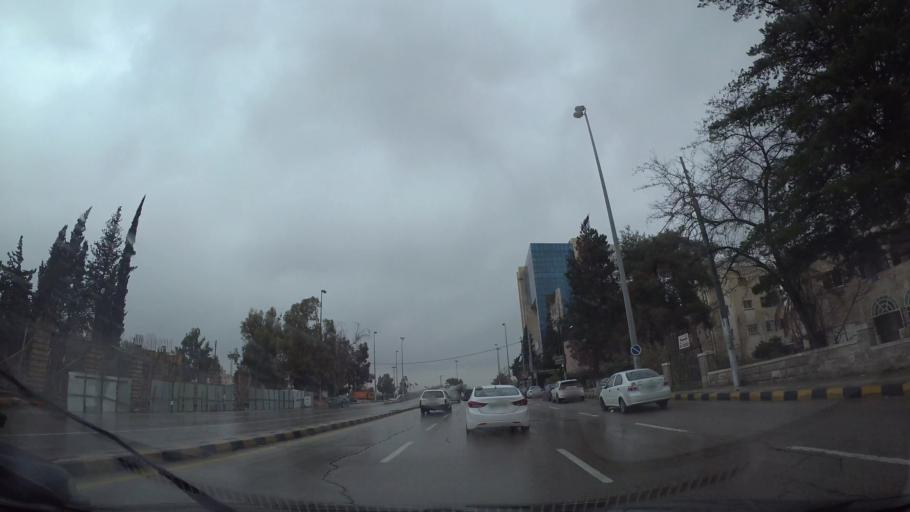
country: JO
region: Amman
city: Amman
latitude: 31.9706
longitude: 35.9092
